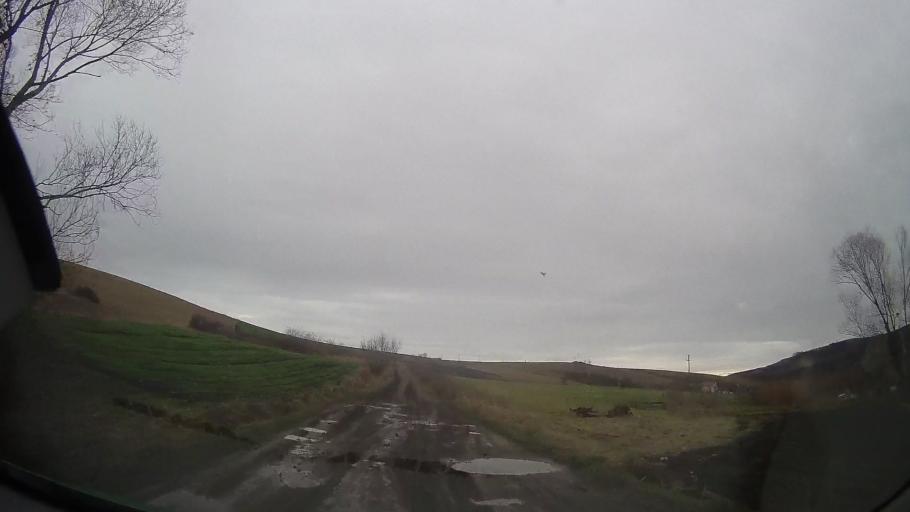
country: RO
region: Mures
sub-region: Comuna Bala
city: Bala
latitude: 46.6953
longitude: 24.4895
